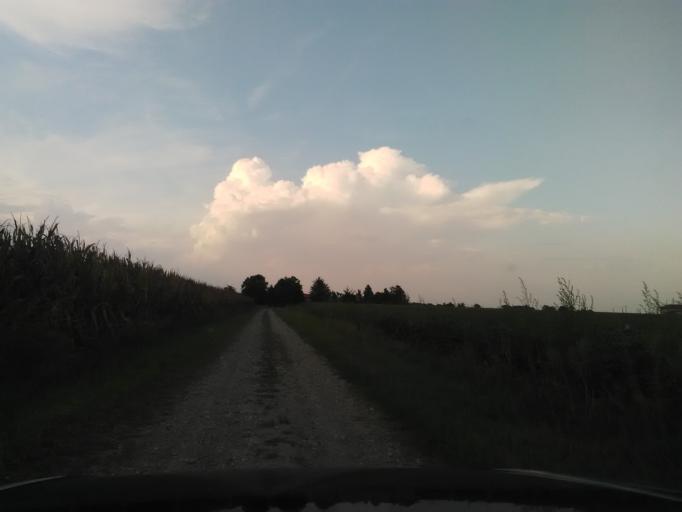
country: IT
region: Piedmont
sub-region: Provincia di Vercelli
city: Cigliano
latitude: 45.3119
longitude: 8.0445
